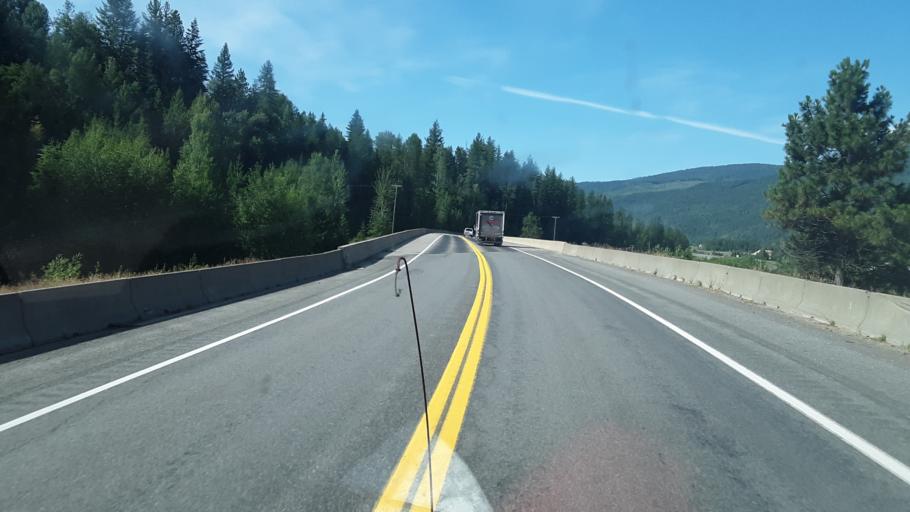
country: US
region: Idaho
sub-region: Bonner County
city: Ponderay
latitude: 48.4140
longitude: -116.5166
